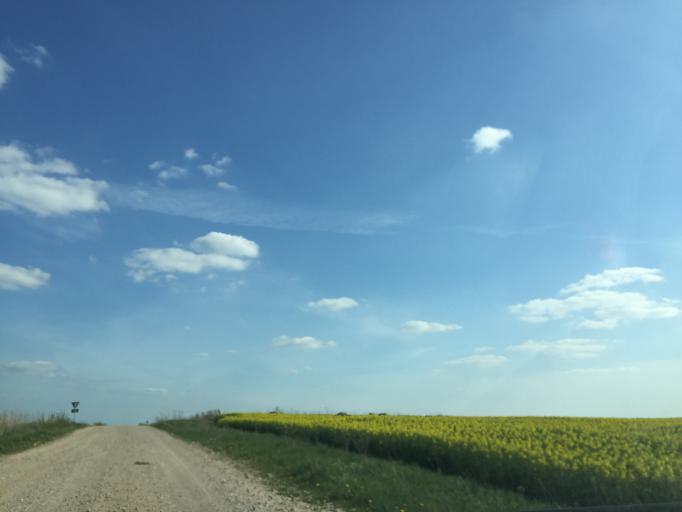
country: LV
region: Bauskas Rajons
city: Bauska
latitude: 56.4853
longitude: 24.3301
